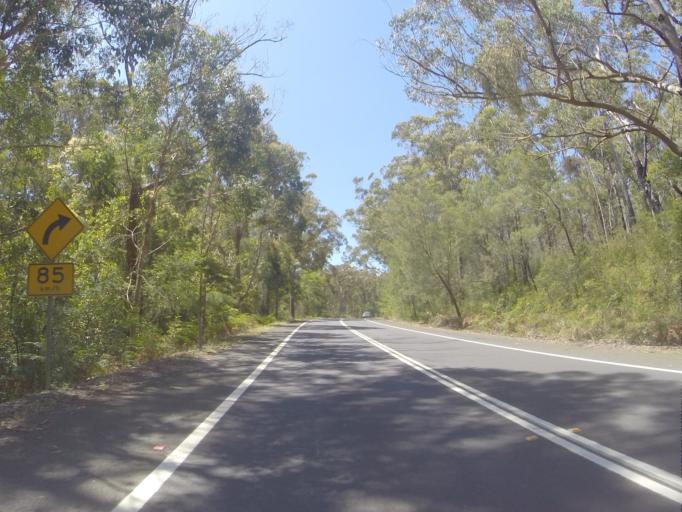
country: AU
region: New South Wales
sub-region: Eurobodalla
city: Batemans Bay
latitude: -35.5325
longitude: 150.3036
